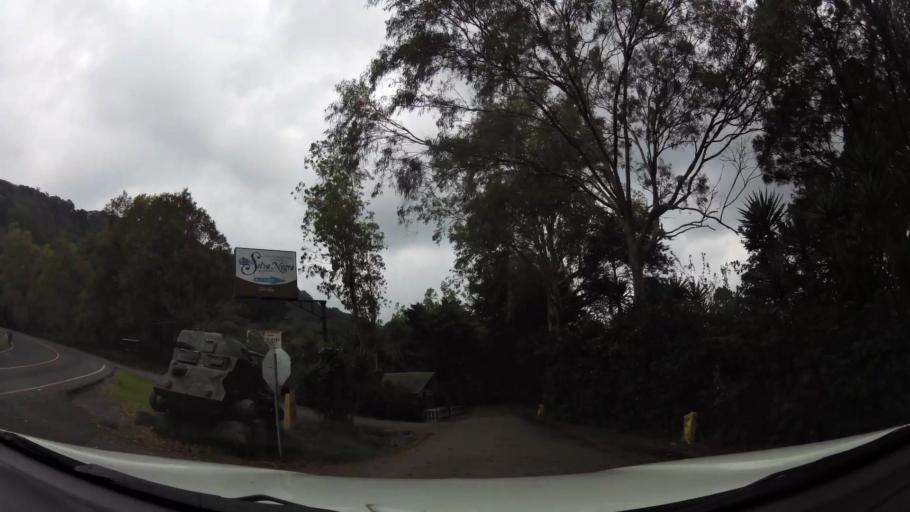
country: NI
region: Matagalpa
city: Matagalpa
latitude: 12.9972
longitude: -85.9210
